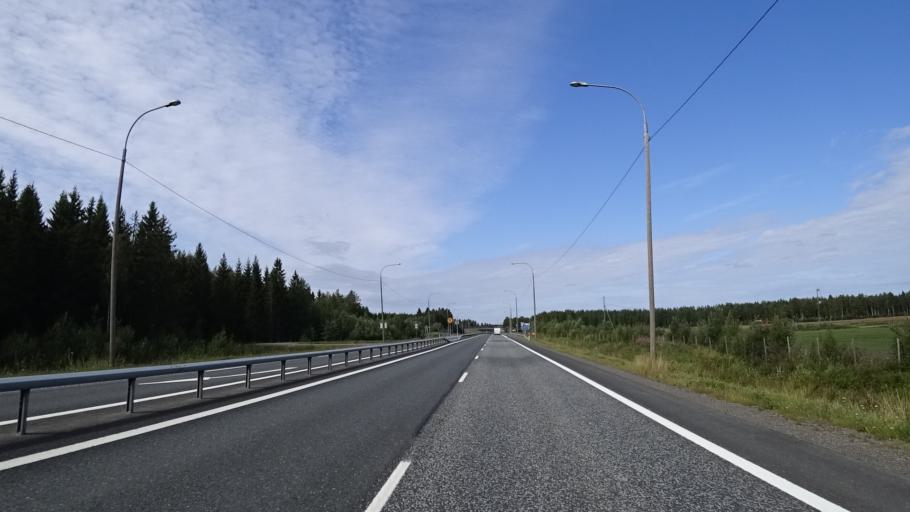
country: FI
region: North Karelia
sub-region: Joensuu
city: Joensuu
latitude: 62.5371
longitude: 29.8542
